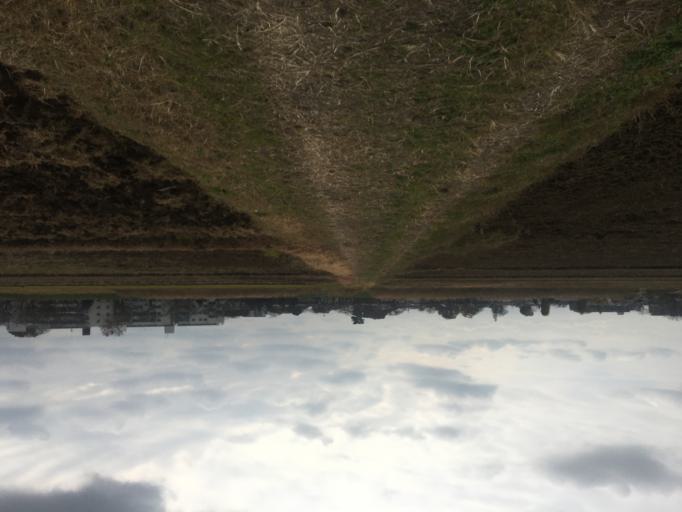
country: JP
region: Saitama
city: Shiki
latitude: 35.8371
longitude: 139.5683
